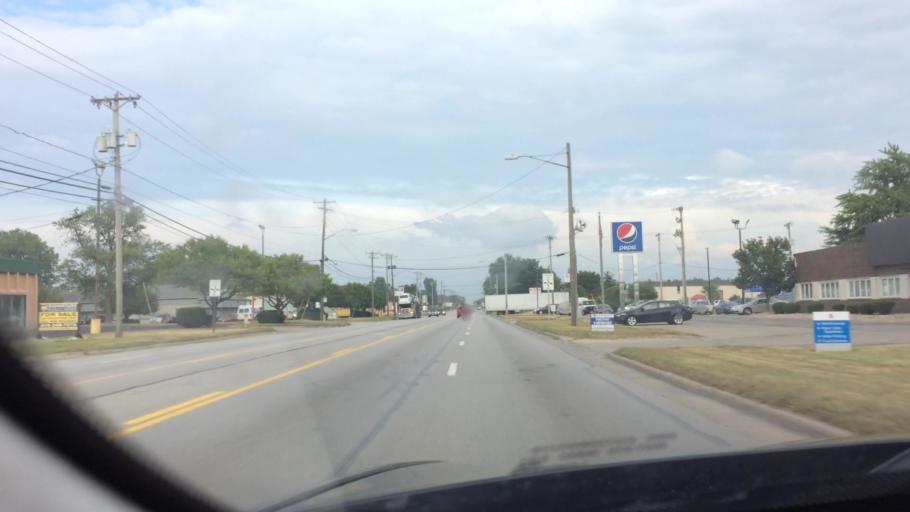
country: US
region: Ohio
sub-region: Lucas County
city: Ottawa Hills
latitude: 41.6380
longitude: -83.6207
